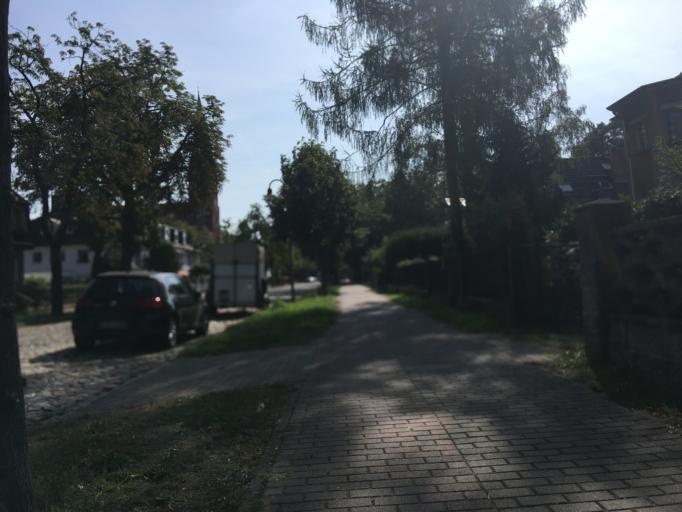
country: DE
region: Brandenburg
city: Zeuthen
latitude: 52.3764
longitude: 13.6176
